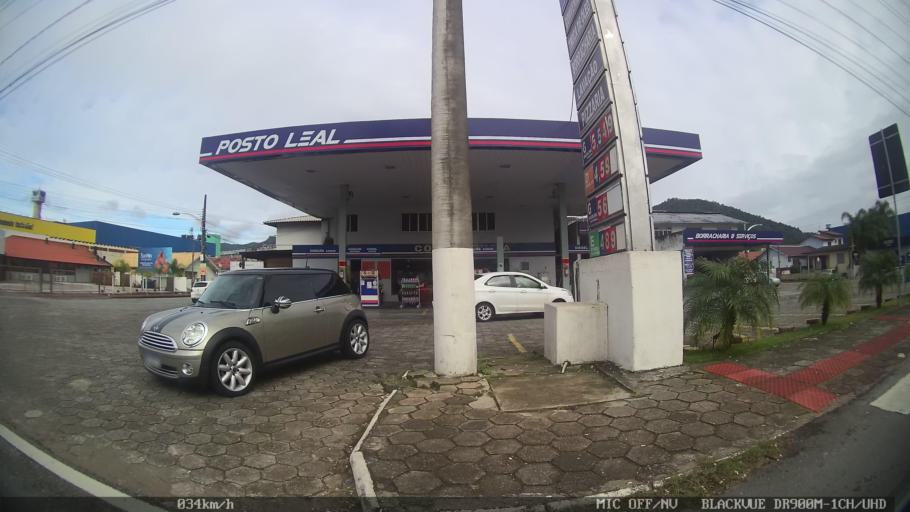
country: BR
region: Santa Catarina
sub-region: Biguacu
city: Biguacu
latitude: -27.4994
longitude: -48.6561
